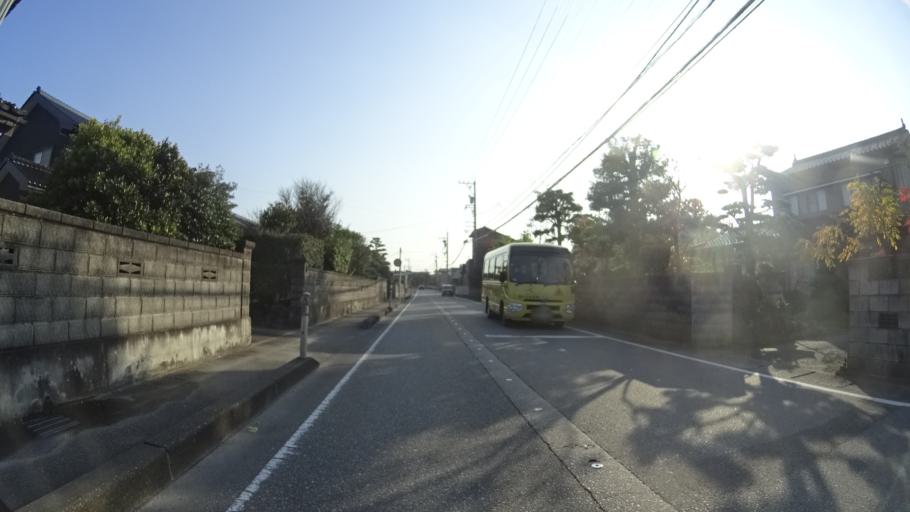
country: JP
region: Toyama
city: Toyama-shi
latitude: 36.6886
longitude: 137.2711
